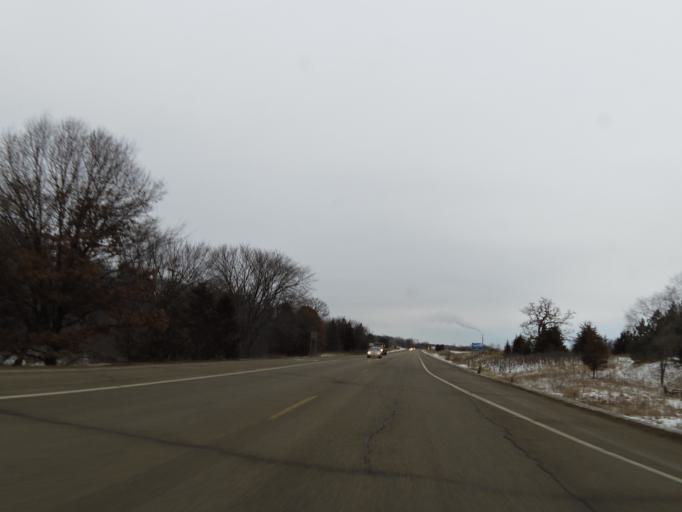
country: US
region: Wisconsin
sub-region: Saint Croix County
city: Hudson
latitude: 44.9802
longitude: -92.7774
